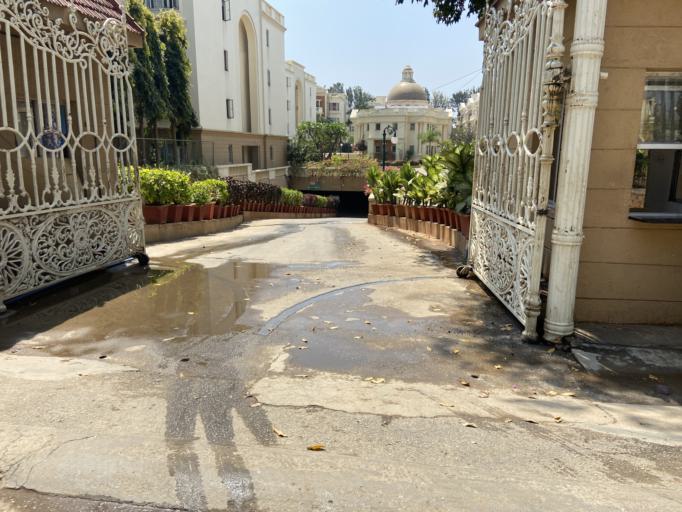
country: IN
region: Karnataka
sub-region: Bangalore Urban
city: Bangalore
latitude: 12.9690
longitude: 77.6845
